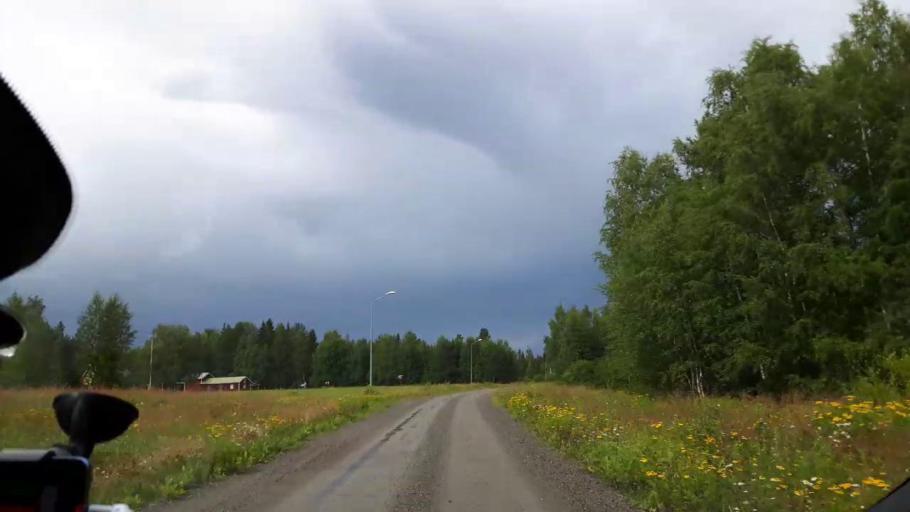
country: SE
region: Jaemtland
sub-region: Stroemsunds Kommun
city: Stroemsund
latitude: 64.0575
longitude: 15.8907
